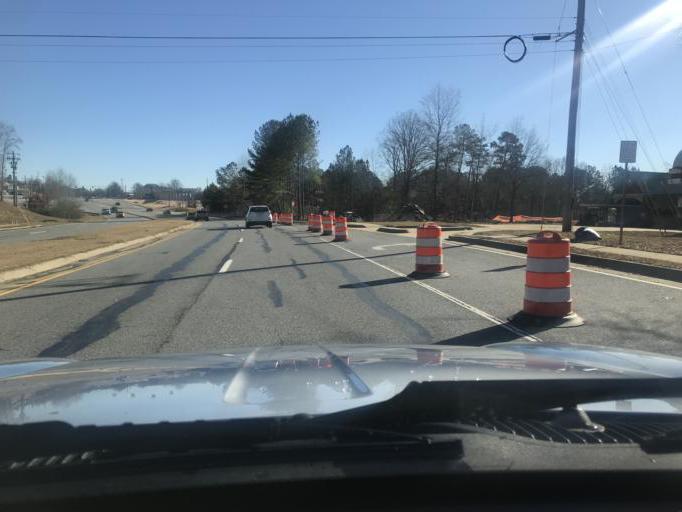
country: US
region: Georgia
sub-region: Gwinnett County
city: Lawrenceville
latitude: 33.9676
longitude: -84.0398
